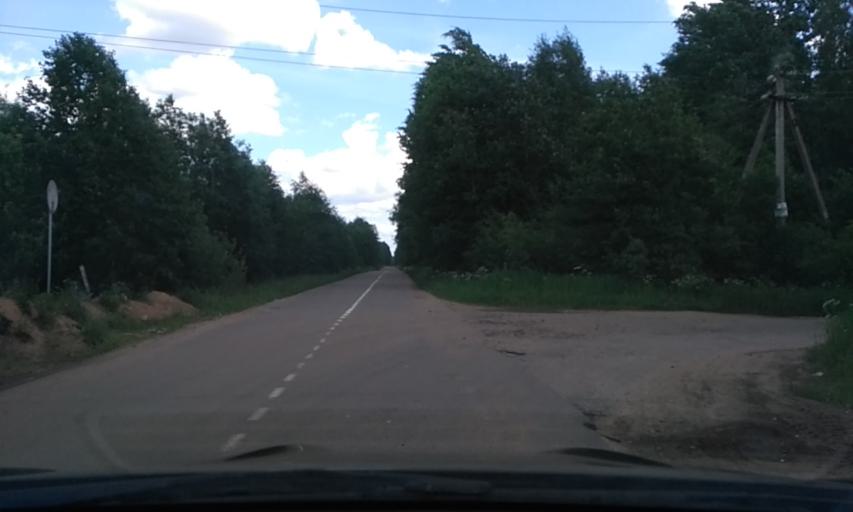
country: RU
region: Leningrad
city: Otradnoye
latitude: 59.8191
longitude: 30.8249
